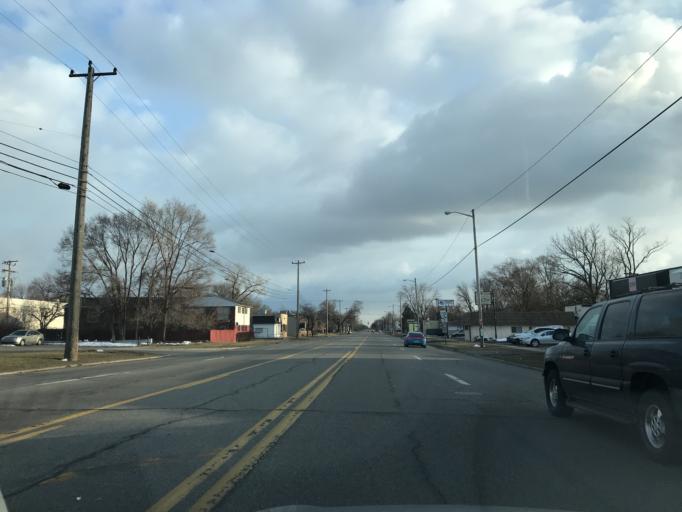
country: US
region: Michigan
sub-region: Wayne County
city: Redford
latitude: 42.4320
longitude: -83.2972
